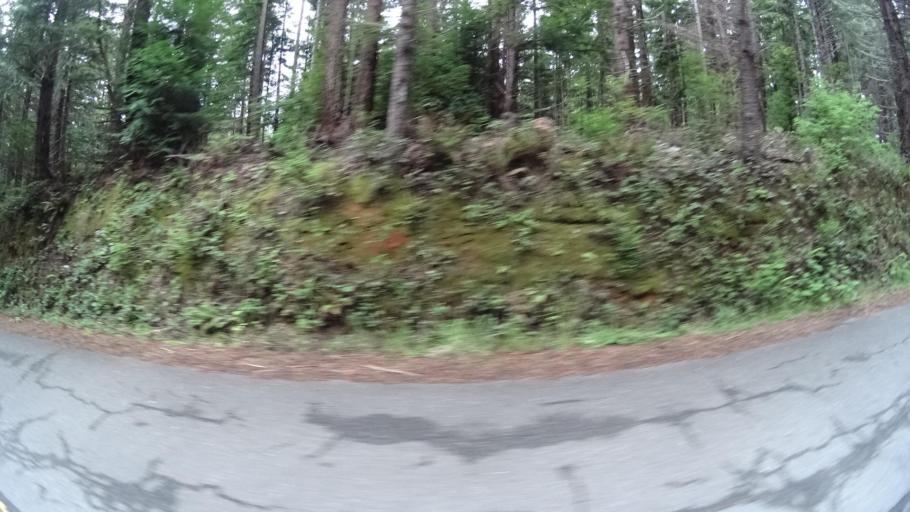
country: US
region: California
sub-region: Humboldt County
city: Blue Lake
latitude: 40.8816
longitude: -123.9709
